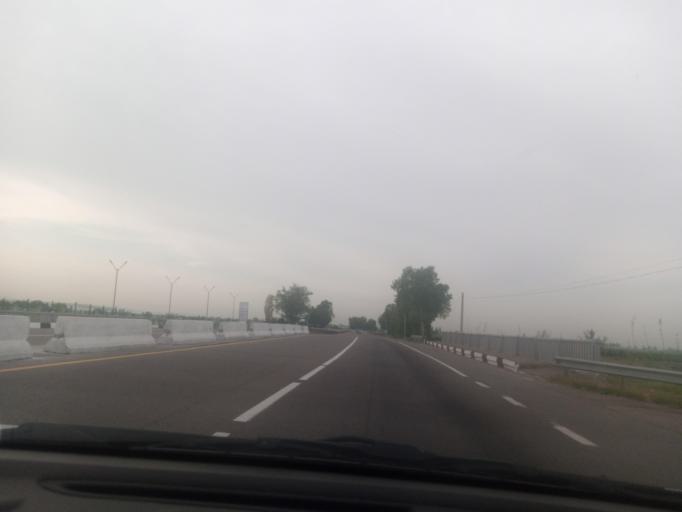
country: UZ
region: Toshkent Shahri
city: Bektemir
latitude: 41.1483
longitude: 69.4288
